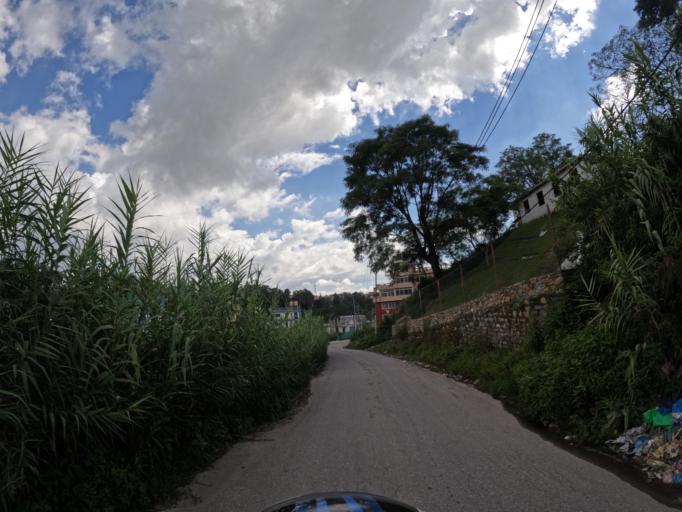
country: NP
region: Central Region
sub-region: Bagmati Zone
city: Kathmandu
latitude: 27.7664
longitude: 85.3269
